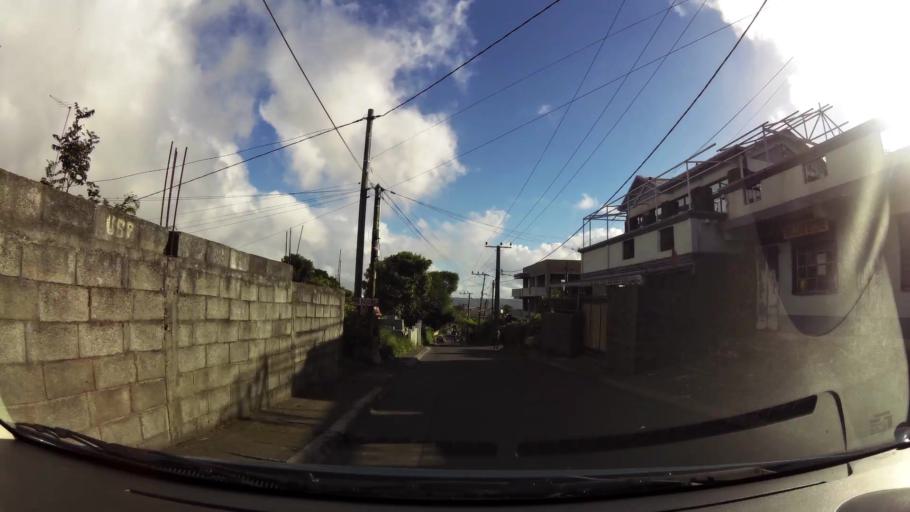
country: MU
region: Plaines Wilhems
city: Curepipe
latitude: -20.3244
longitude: 57.5081
